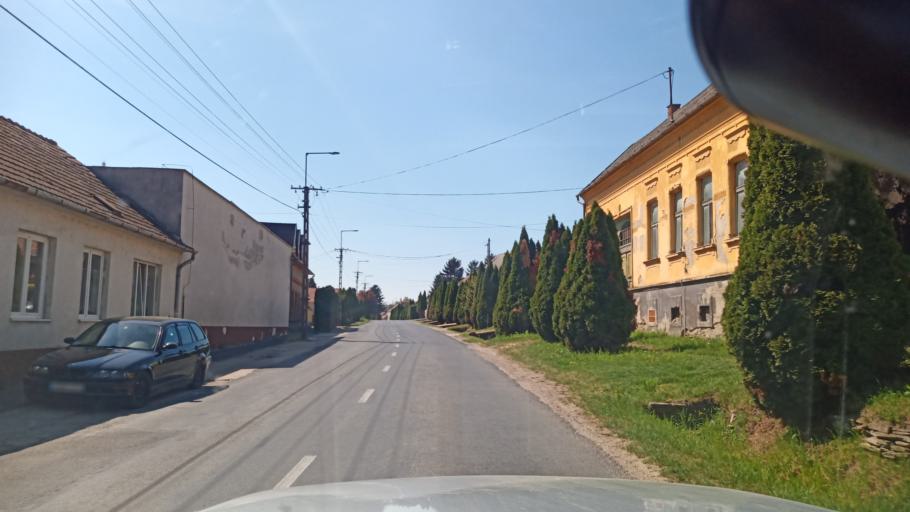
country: HU
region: Zala
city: Sarmellek
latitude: 46.7331
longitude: 17.1063
